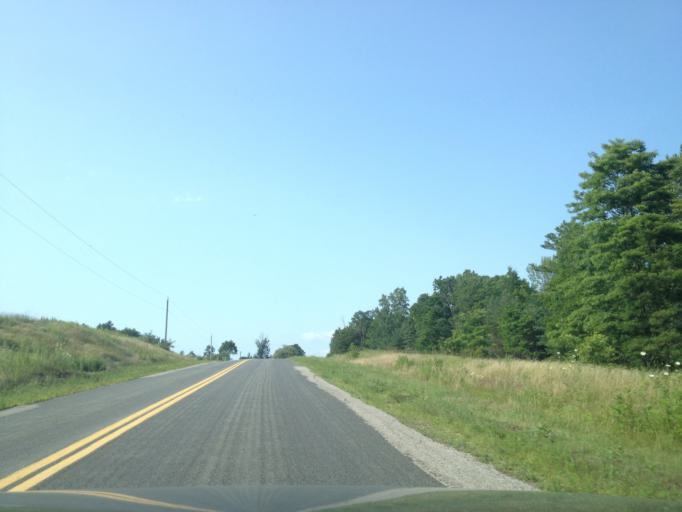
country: CA
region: Ontario
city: Aylmer
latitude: 42.7345
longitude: -80.8536
